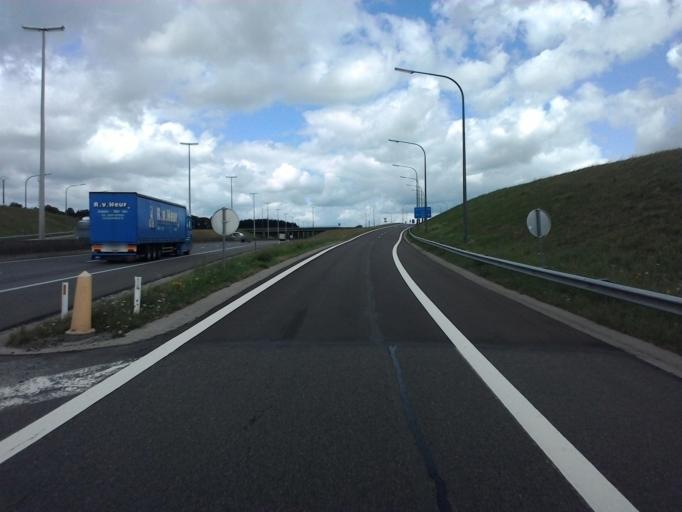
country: BE
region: Wallonia
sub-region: Province du Luxembourg
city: Leglise
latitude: 49.8051
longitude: 5.5191
